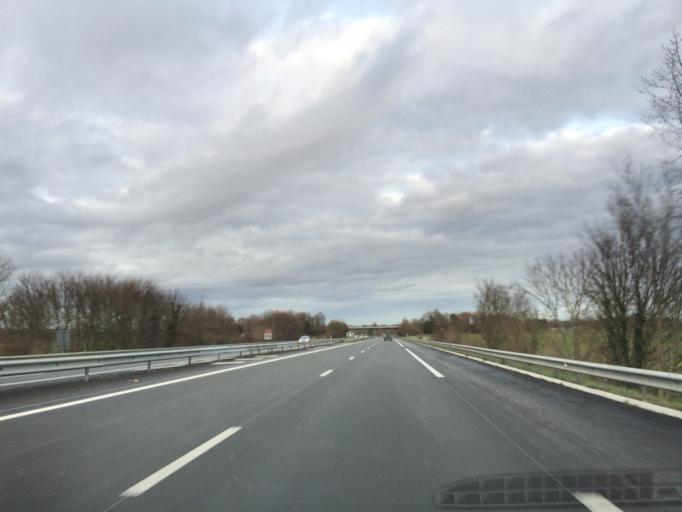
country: FR
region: Poitou-Charentes
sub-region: Departement des Deux-Sevres
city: Aiffres
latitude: 46.2668
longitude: -0.4112
